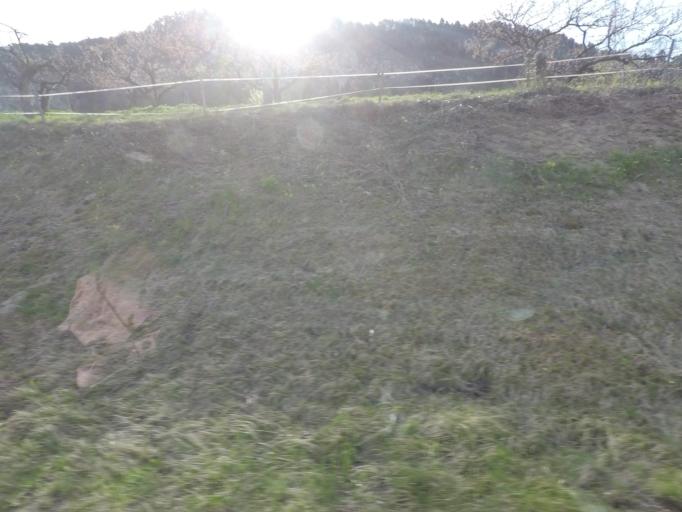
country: CH
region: Valais
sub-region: Herens District
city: Vex
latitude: 46.2222
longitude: 7.3880
